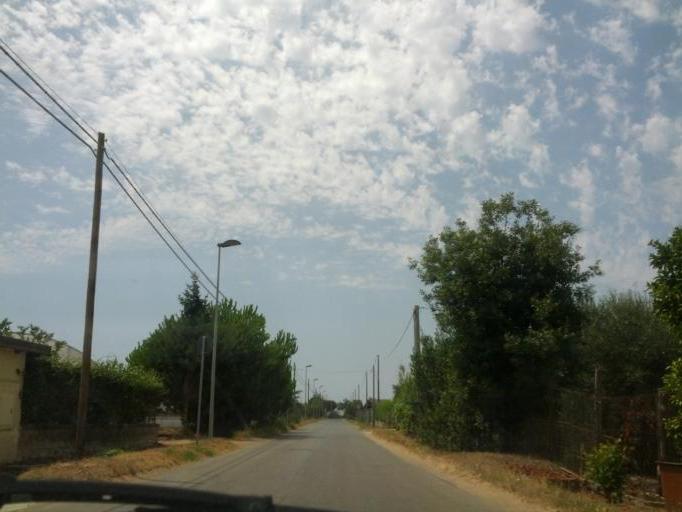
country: IT
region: Latium
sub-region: Provincia di Latina
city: Sperlonga
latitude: 41.2915
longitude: 13.3962
